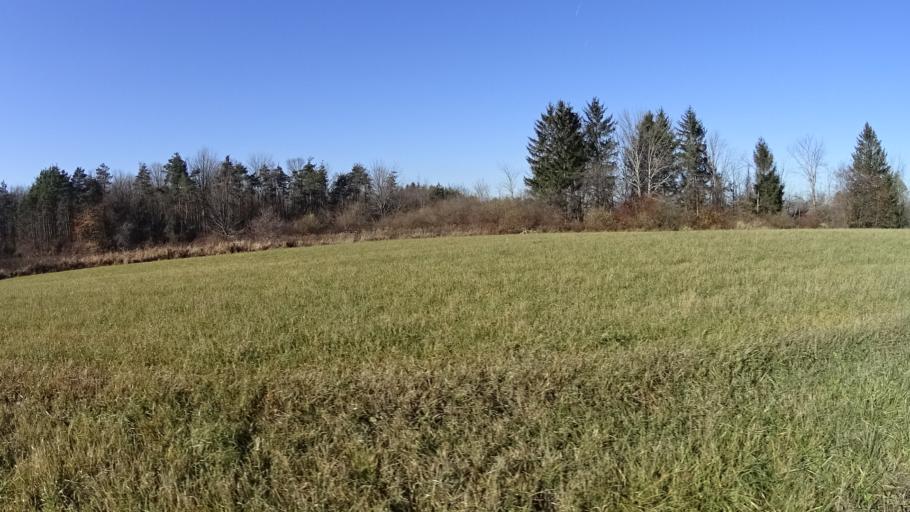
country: US
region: Ohio
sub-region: Lorain County
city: Wellington
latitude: 41.0671
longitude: -82.1815
